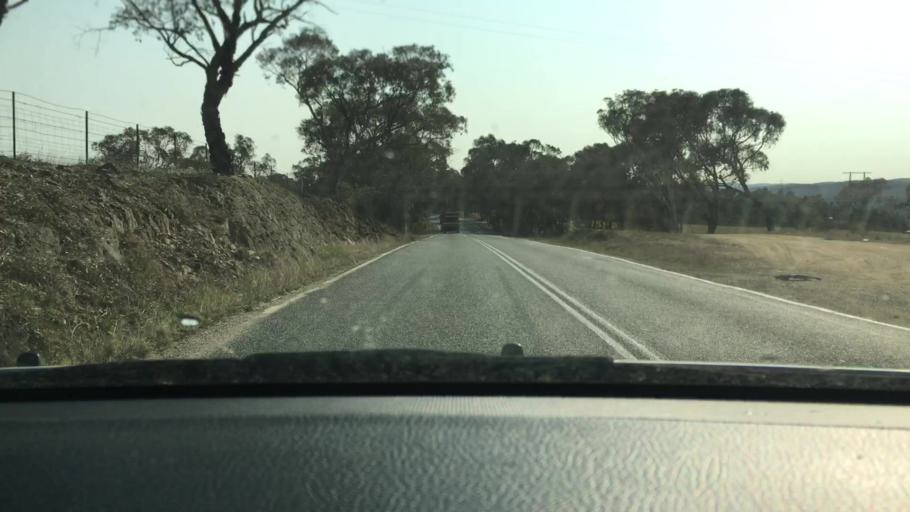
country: AU
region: New South Wales
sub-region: Queanbeyan
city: Queanbeyan
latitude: -35.4072
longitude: 149.2277
